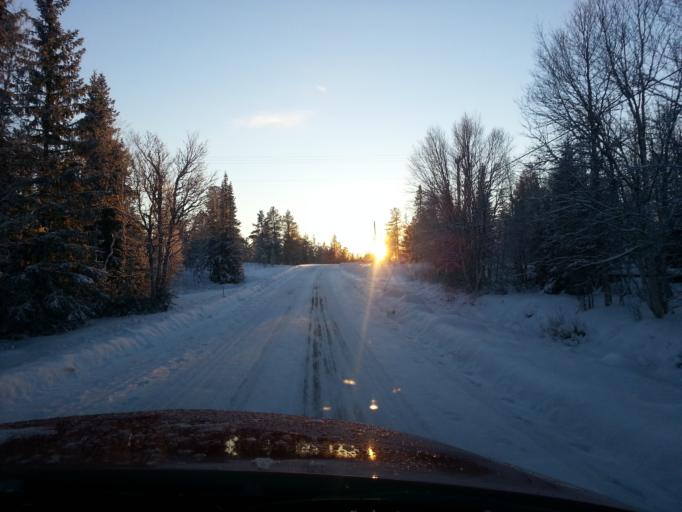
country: SE
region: Jaemtland
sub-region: Harjedalens Kommun
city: Sveg
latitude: 62.2849
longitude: 13.3981
